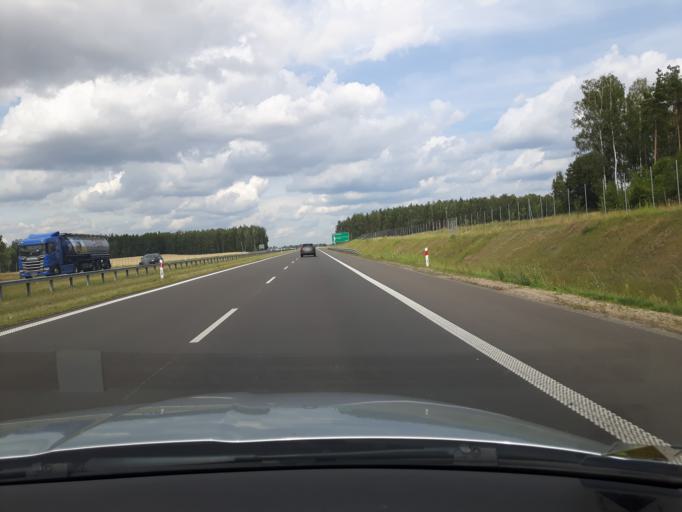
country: PL
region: Masovian Voivodeship
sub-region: Powiat mlawski
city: Wieczfnia Koscielna
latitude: 53.2672
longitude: 20.4314
